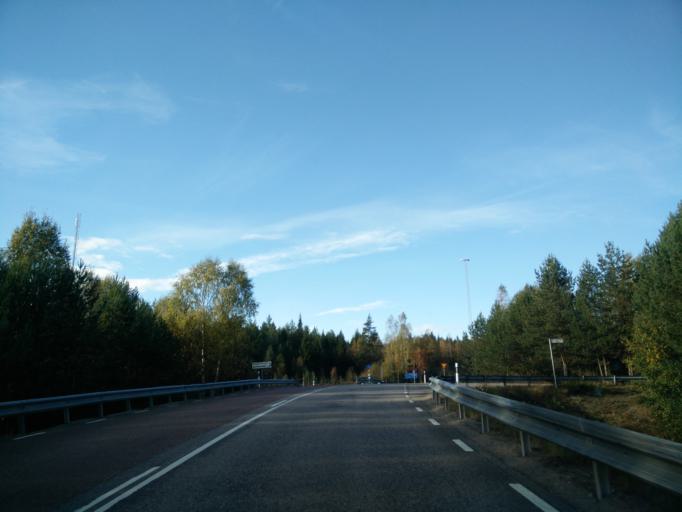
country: SE
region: Gaevleborg
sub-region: Hudiksvalls Kommun
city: Hudiksvall
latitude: 61.7762
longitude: 17.1214
